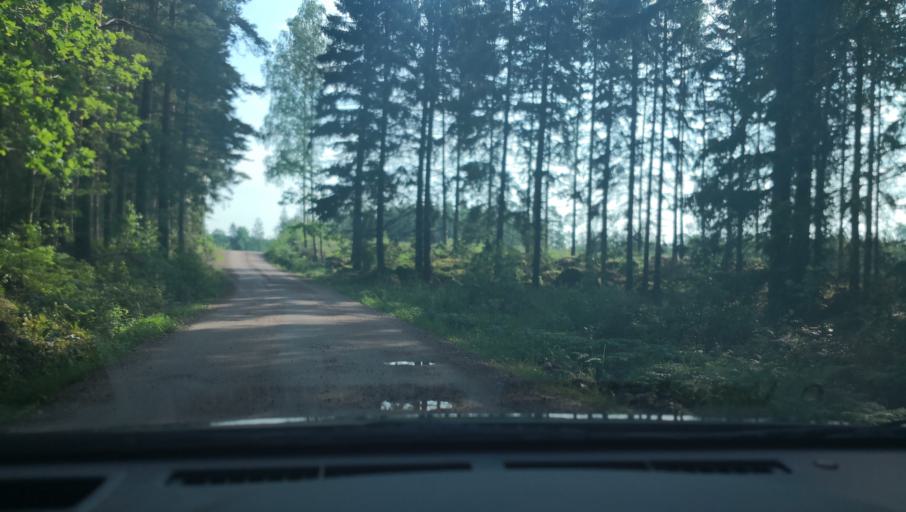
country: SE
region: Vaestmanland
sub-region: Arboga Kommun
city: Tyringe
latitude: 59.3135
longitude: 15.9932
